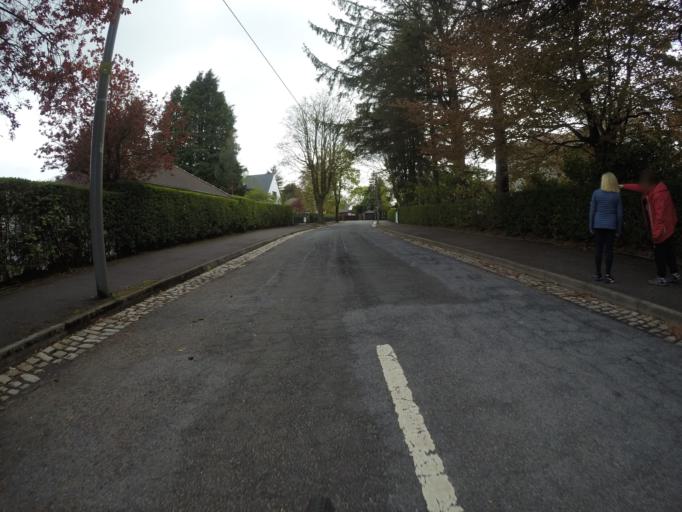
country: GB
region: Scotland
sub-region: East Renfrewshire
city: Giffnock
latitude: 55.7833
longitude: -4.3064
